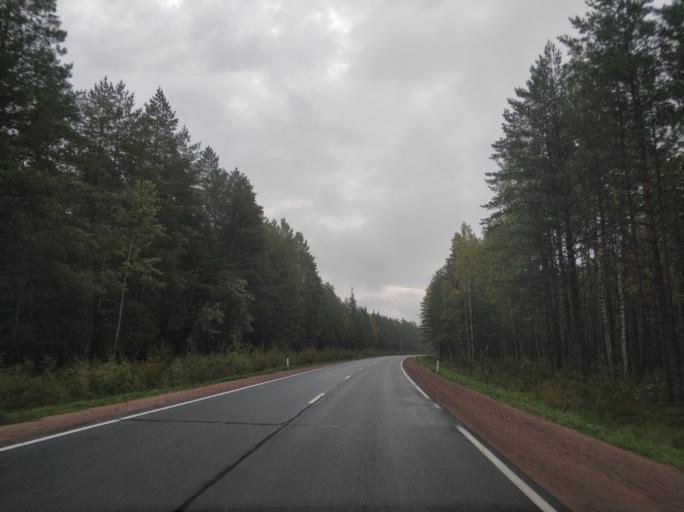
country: RU
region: Leningrad
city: Shcheglovo
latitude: 60.1029
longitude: 30.8169
